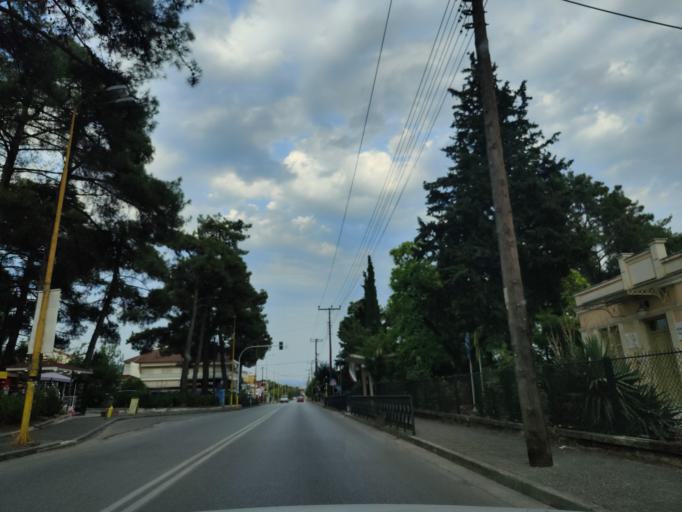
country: GR
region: East Macedonia and Thrace
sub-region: Nomos Dramas
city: Drama
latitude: 41.1534
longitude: 24.1222
